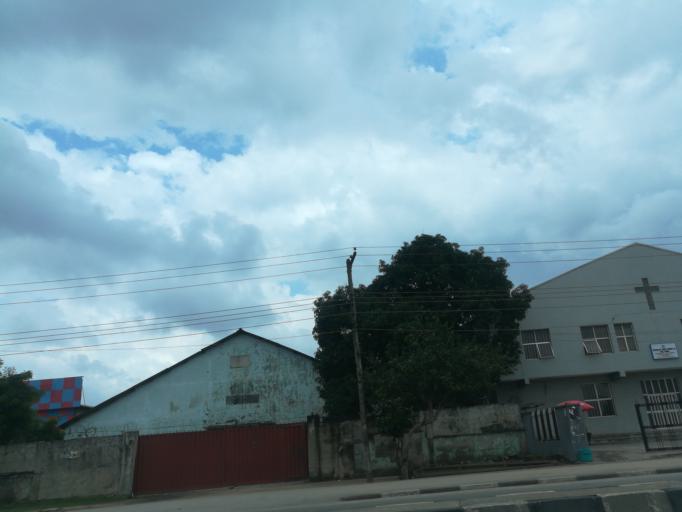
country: NG
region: Lagos
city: Mushin
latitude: 6.5403
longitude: 3.3560
